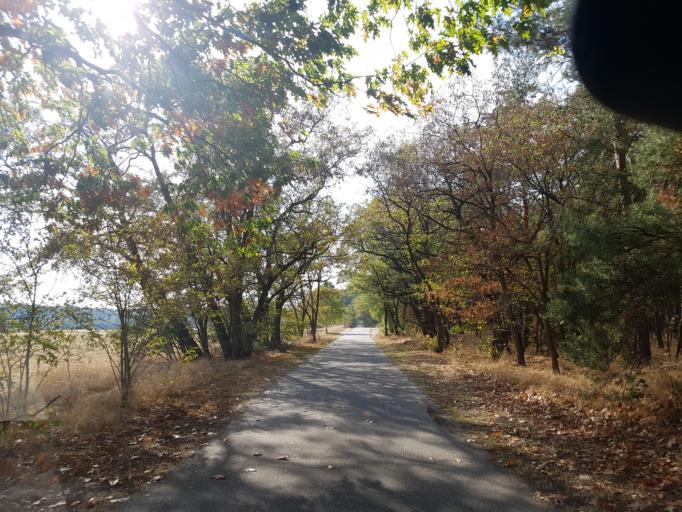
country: DE
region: Brandenburg
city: Hohenbucko
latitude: 51.6897
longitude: 13.4614
